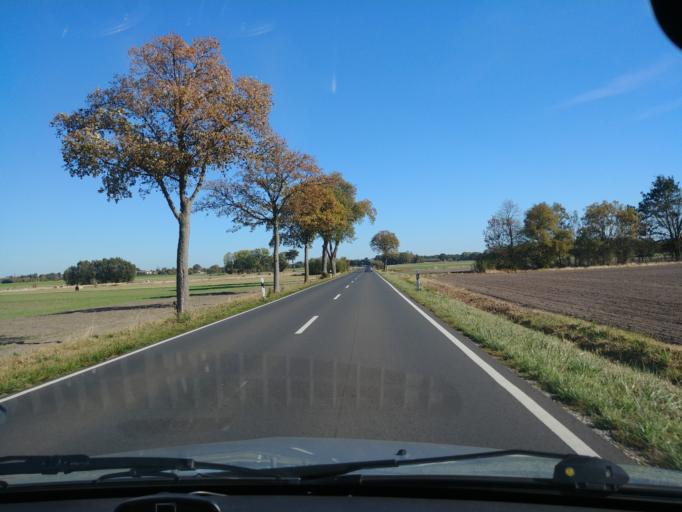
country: DE
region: Lower Saxony
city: Leiferde
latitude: 52.4235
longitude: 10.4239
